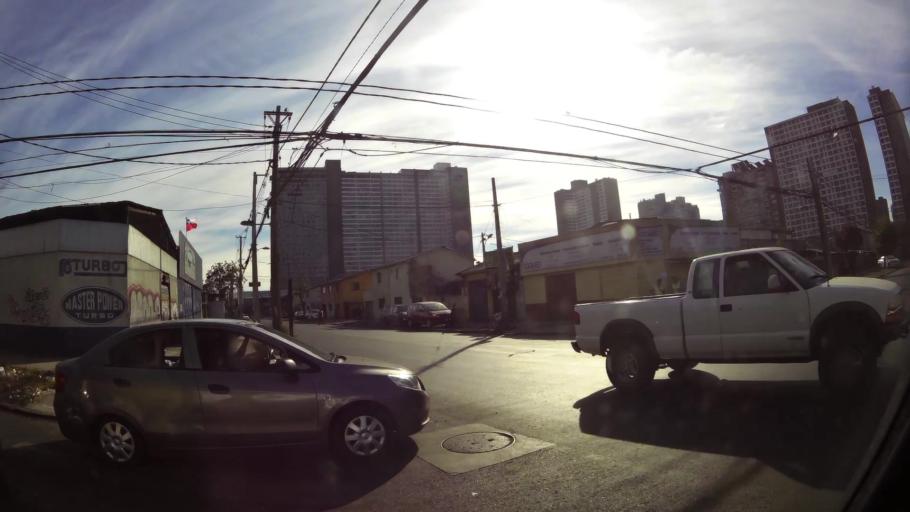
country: CL
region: Santiago Metropolitan
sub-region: Provincia de Santiago
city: Santiago
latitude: -33.4575
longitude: -70.6880
